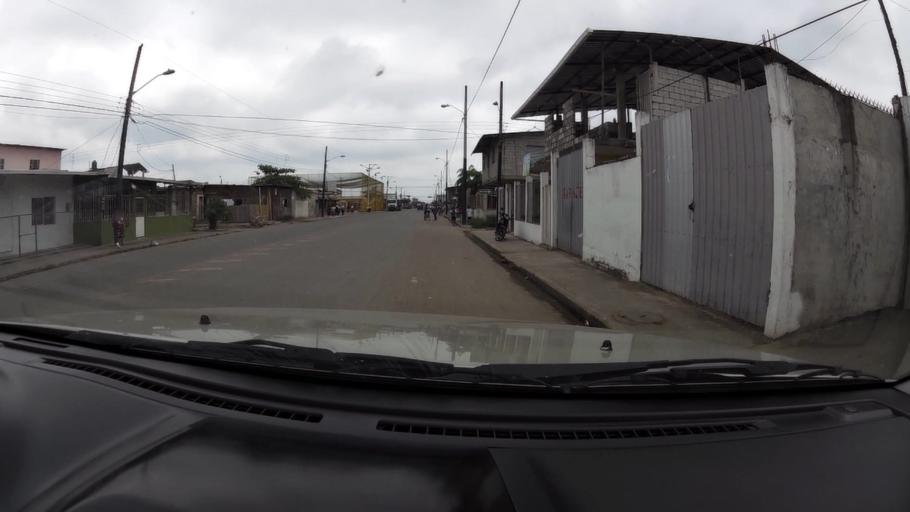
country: EC
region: El Oro
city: Pasaje
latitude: -3.2389
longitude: -79.8288
